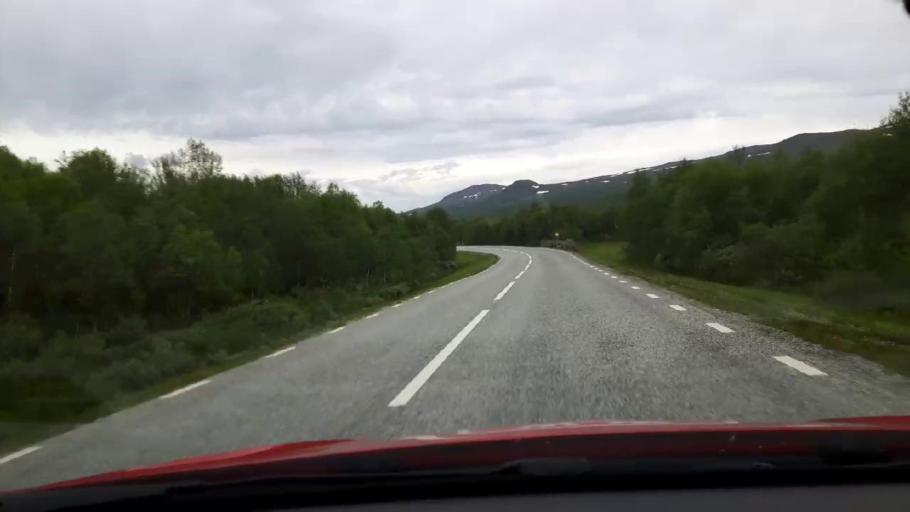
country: NO
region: Sor-Trondelag
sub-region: Tydal
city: Aas
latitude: 62.6180
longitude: 12.1354
